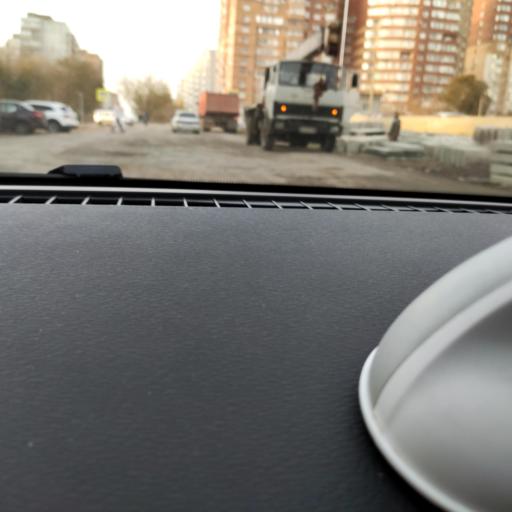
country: RU
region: Samara
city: Samara
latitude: 53.1957
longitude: 50.1483
